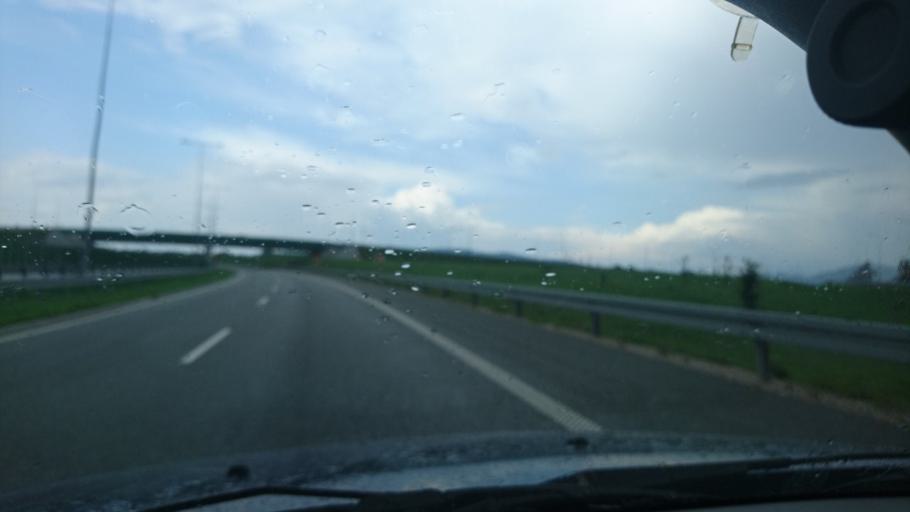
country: PL
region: Silesian Voivodeship
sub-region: Powiat zywiecki
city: Pietrzykowice
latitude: 49.6803
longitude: 19.1685
